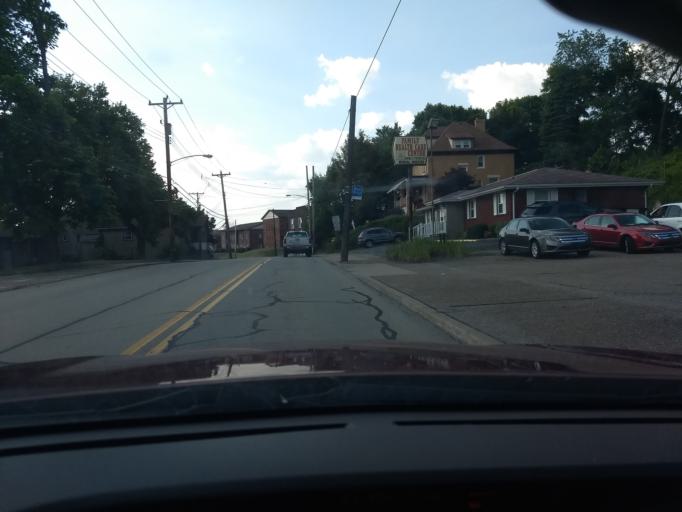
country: US
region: Pennsylvania
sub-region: Allegheny County
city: Versailles
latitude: 40.3182
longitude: -79.8340
